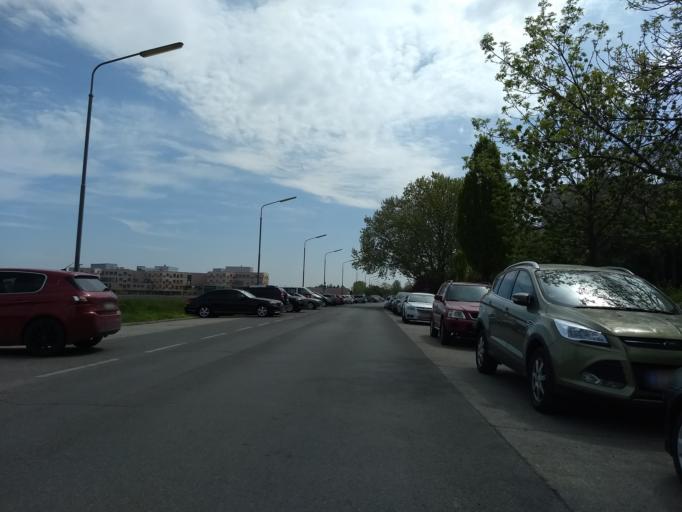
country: AT
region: Lower Austria
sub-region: Politischer Bezirk Wien-Umgebung
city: Gerasdorf bei Wien
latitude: 48.2417
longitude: 16.4843
